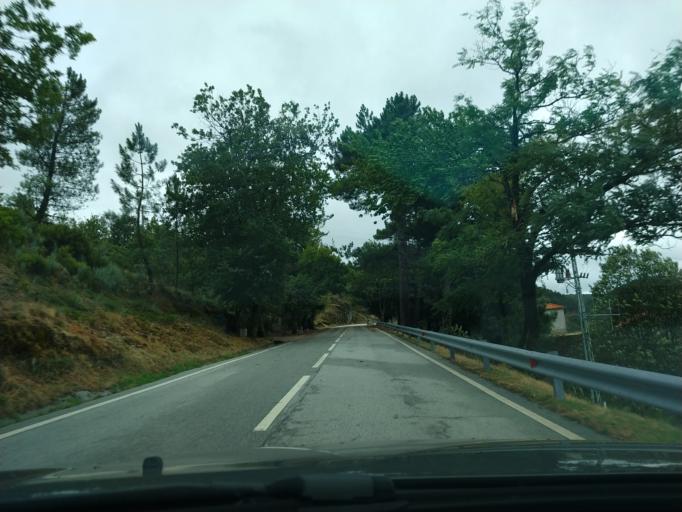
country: PT
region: Guarda
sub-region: Seia
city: Seia
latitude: 40.3170
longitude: -7.6847
